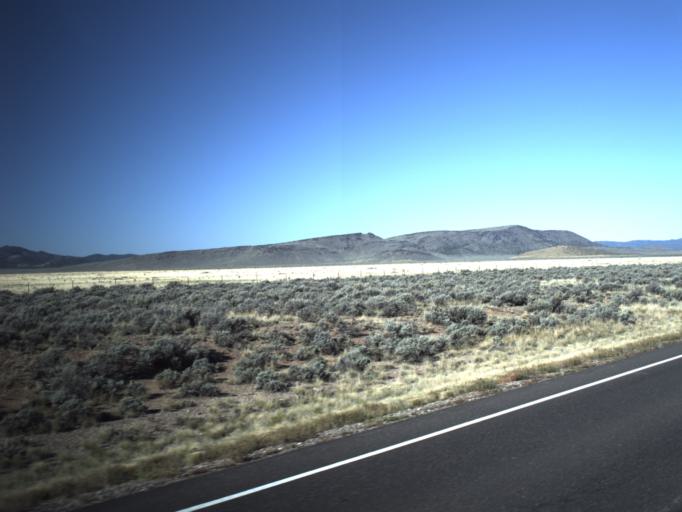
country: US
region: Utah
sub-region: Washington County
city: Enterprise
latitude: 37.7686
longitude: -113.8239
